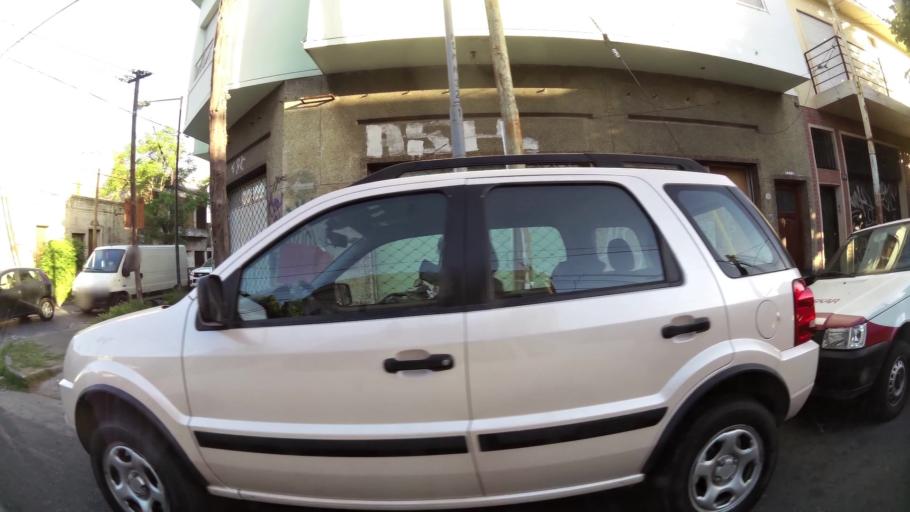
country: AR
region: Buenos Aires
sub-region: Partido de General San Martin
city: General San Martin
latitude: -34.5663
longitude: -58.5426
